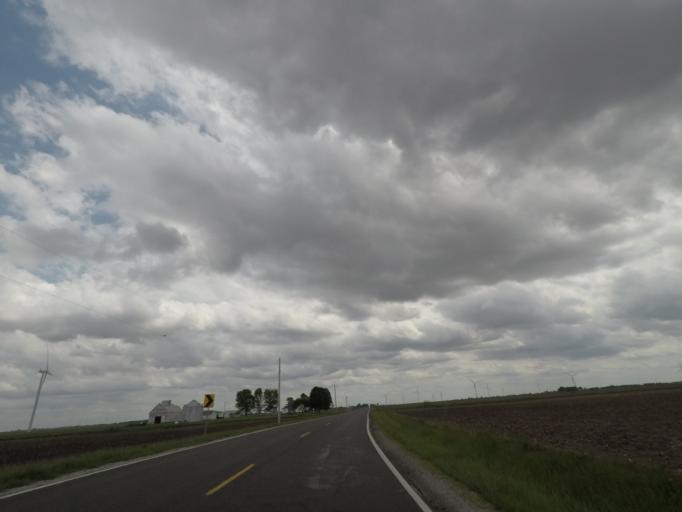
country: US
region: Illinois
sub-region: Macon County
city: Warrensburg
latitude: 40.0483
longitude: -89.0856
